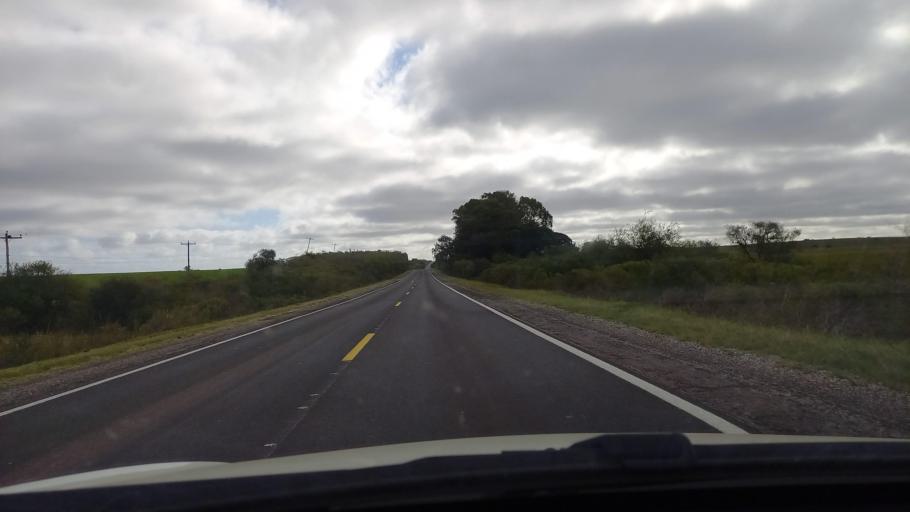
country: BR
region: Rio Grande do Sul
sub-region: Dom Pedrito
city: Dom Pedrito
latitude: -30.9154
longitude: -54.7977
